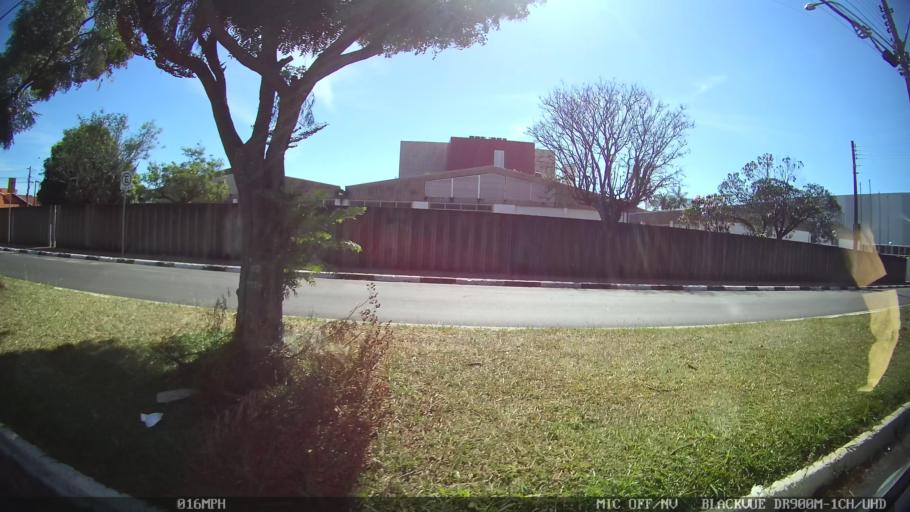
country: BR
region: Sao Paulo
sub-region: Franca
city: Franca
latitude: -20.5439
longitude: -47.3820
